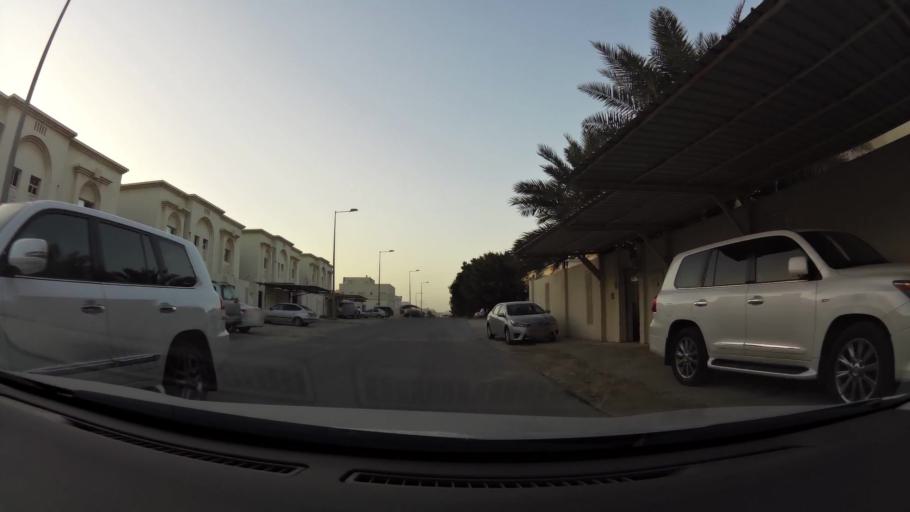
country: QA
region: Baladiyat ar Rayyan
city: Ar Rayyan
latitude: 25.3220
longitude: 51.4651
